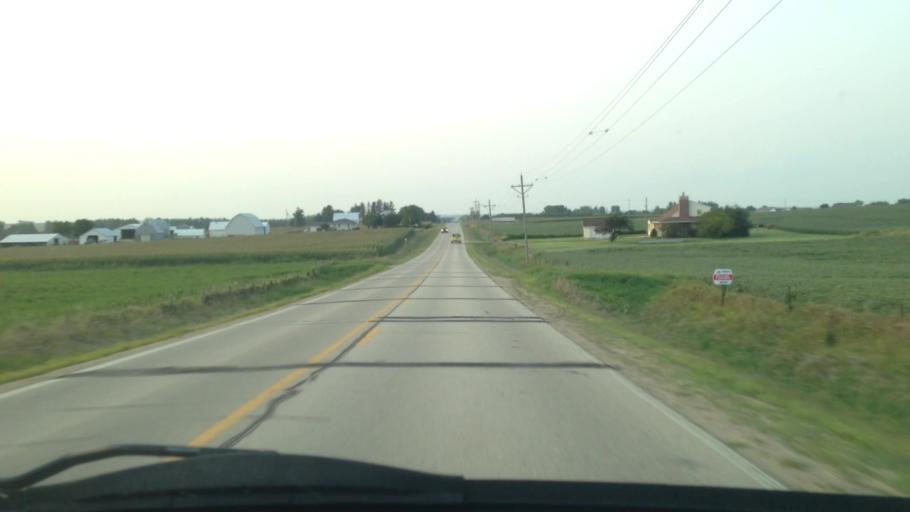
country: US
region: Iowa
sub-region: Benton County
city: Atkins
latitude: 41.9876
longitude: -91.8731
